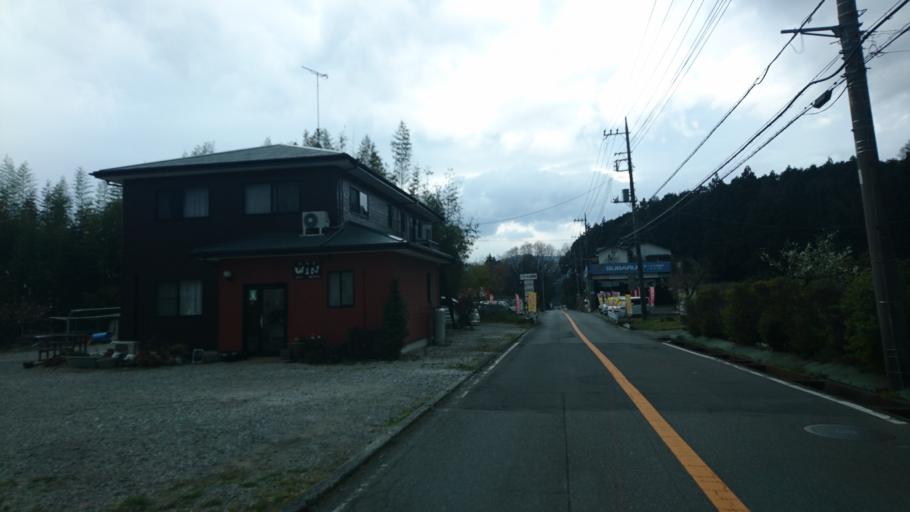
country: JP
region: Shizuoka
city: Fujinomiya
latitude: 35.2634
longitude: 138.6061
